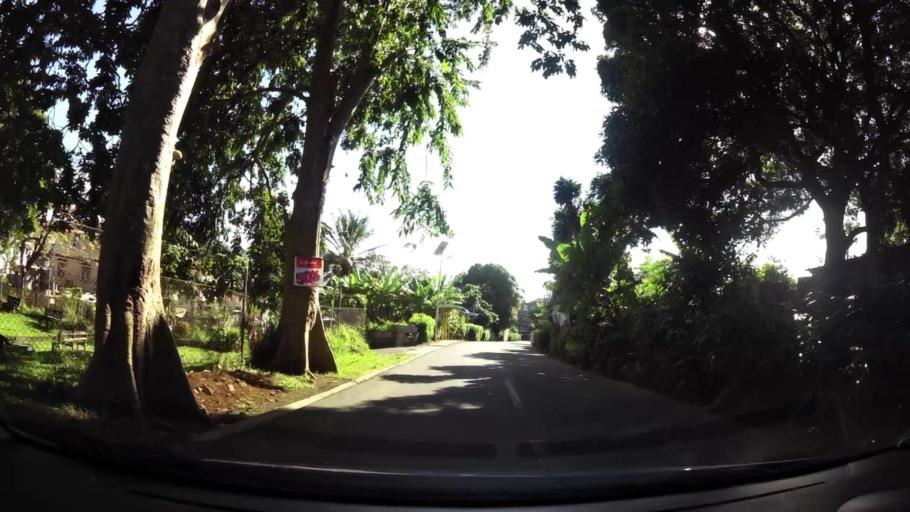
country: MU
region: Grand Port
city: Mahebourg
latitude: -20.4061
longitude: 57.7007
